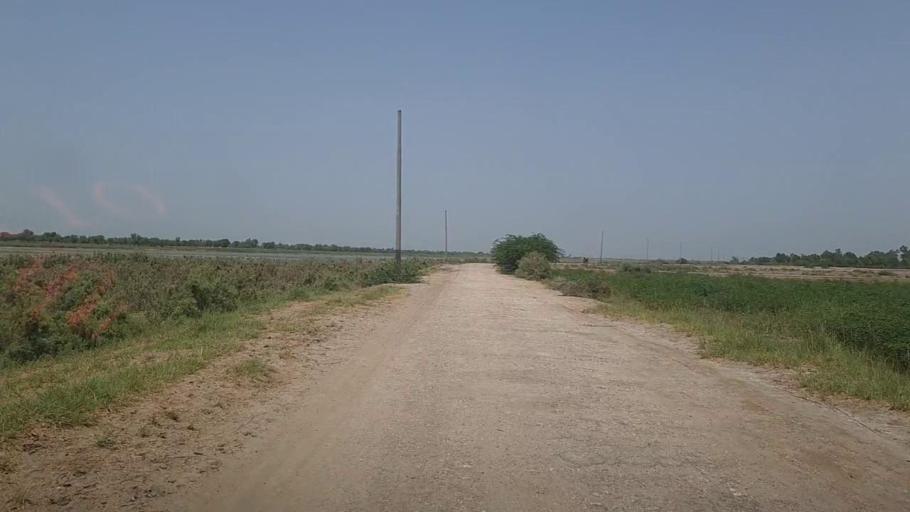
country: PK
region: Sindh
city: Pad Idan
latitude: 26.8524
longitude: 68.2954
